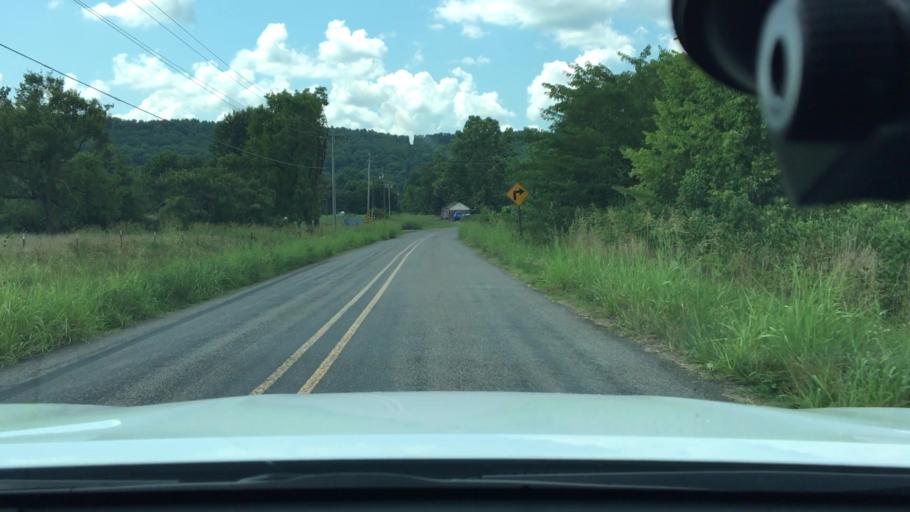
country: US
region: Arkansas
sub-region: Logan County
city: Paris
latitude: 35.2700
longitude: -93.6516
